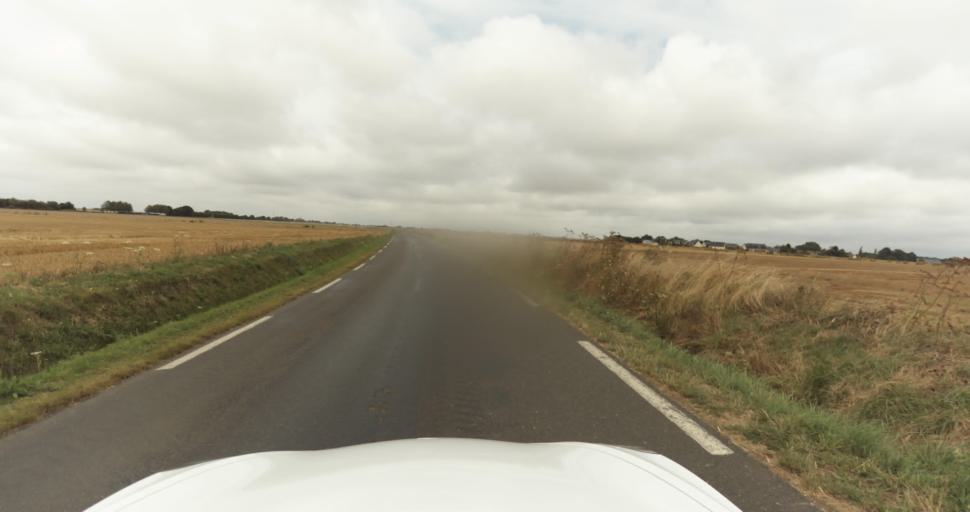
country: FR
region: Haute-Normandie
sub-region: Departement de l'Eure
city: Claville
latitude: 49.0730
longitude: 1.0660
